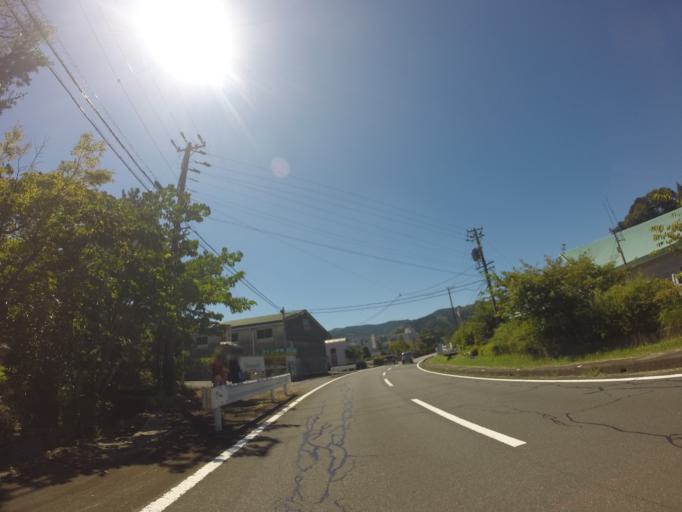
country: JP
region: Shizuoka
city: Fujieda
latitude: 34.9146
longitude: 138.2022
